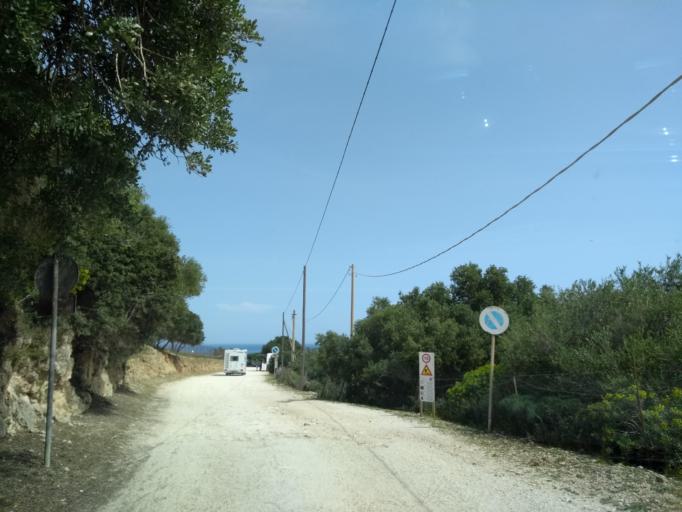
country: IT
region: Sicily
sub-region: Trapani
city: Castelluzzo
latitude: 38.0806
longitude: 12.8079
